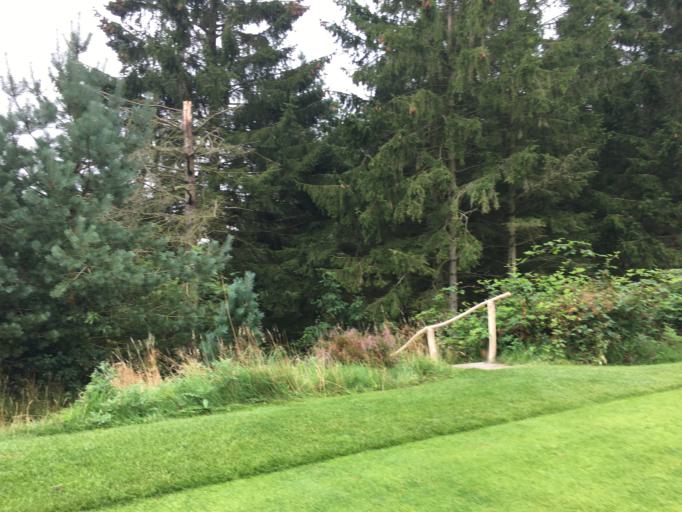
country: DK
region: Central Jutland
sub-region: Holstebro Kommune
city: Ulfborg
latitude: 56.3245
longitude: 8.4328
